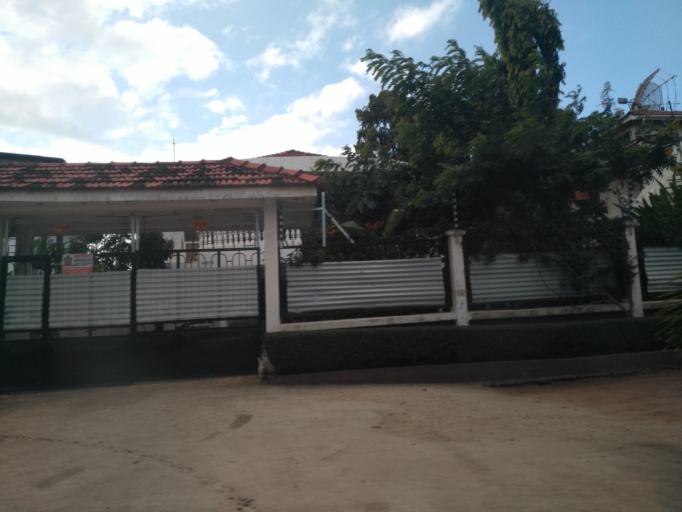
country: TZ
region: Dar es Salaam
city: Magomeni
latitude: -6.7613
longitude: 39.2679
